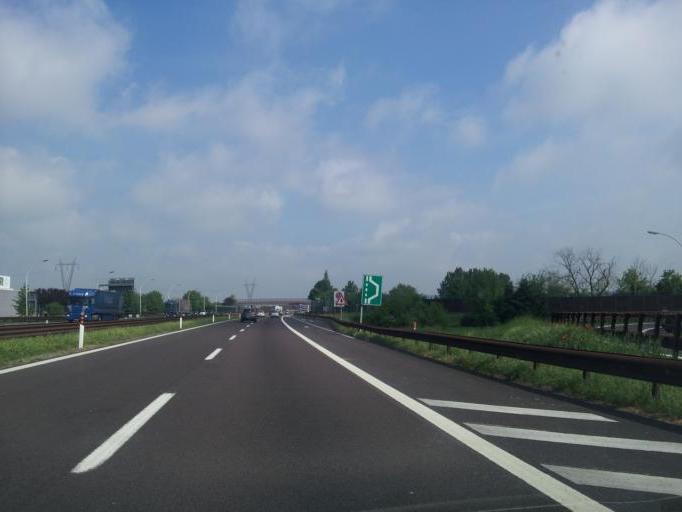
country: IT
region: Lombardy
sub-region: Provincia di Mantova
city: Pegognaga
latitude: 44.9904
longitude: 10.8517
